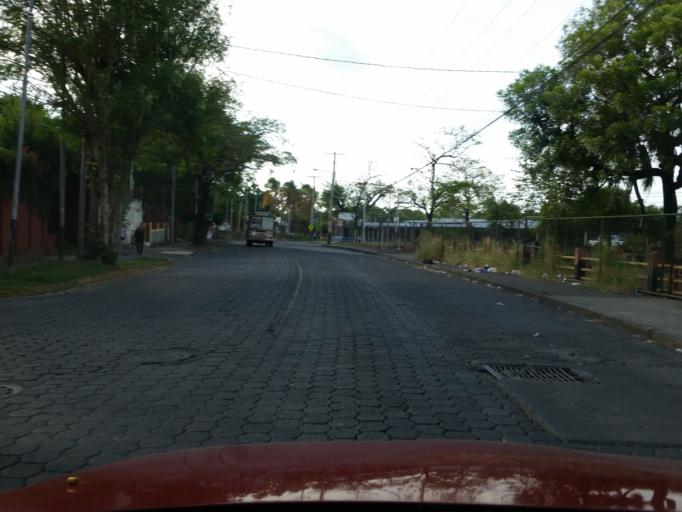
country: NI
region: Managua
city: Managua
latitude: 12.1363
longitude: -86.2656
